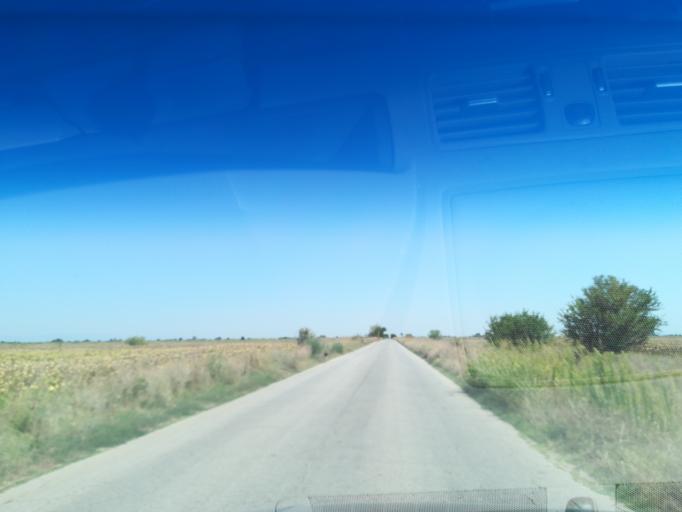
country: BG
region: Plovdiv
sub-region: Obshtina Suedinenie
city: Suedinenie
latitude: 42.2517
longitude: 24.4573
